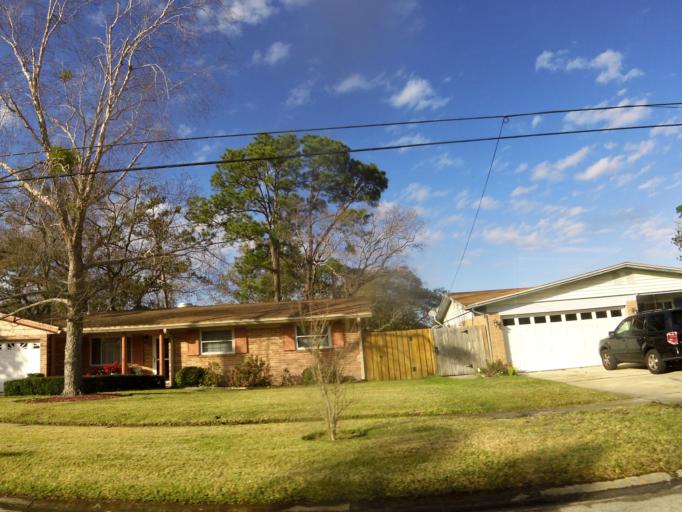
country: US
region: Florida
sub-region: Duval County
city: Jacksonville
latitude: 30.2859
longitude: -81.6077
